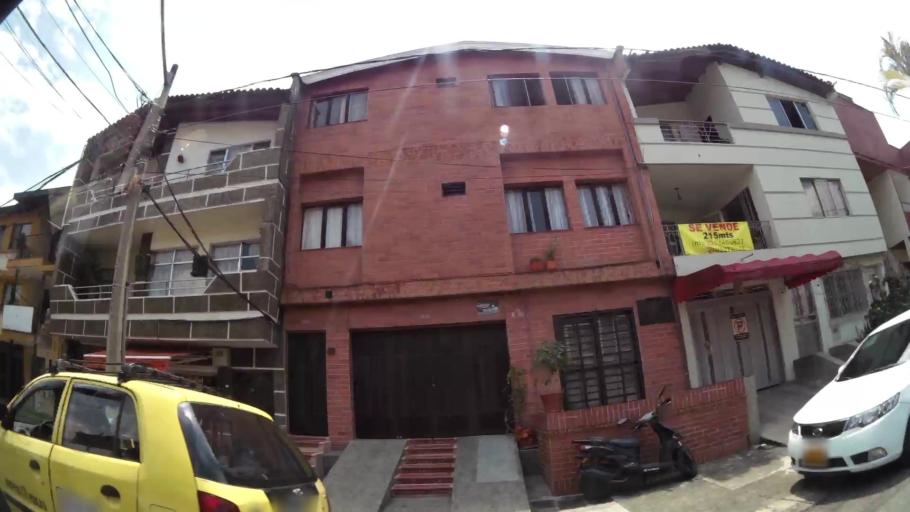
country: CO
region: Antioquia
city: Medellin
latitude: 6.2362
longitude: -75.5987
